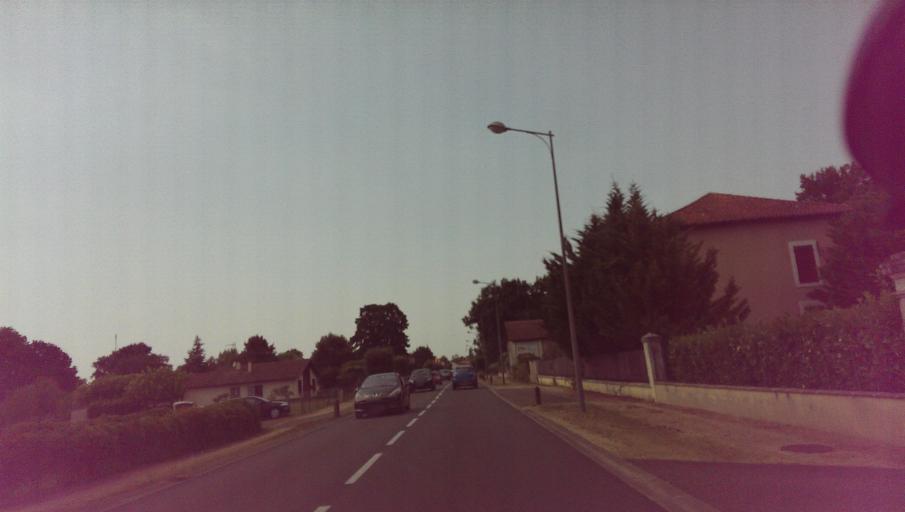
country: FR
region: Aquitaine
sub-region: Departement des Landes
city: Sabres
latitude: 44.1459
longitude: -0.7336
